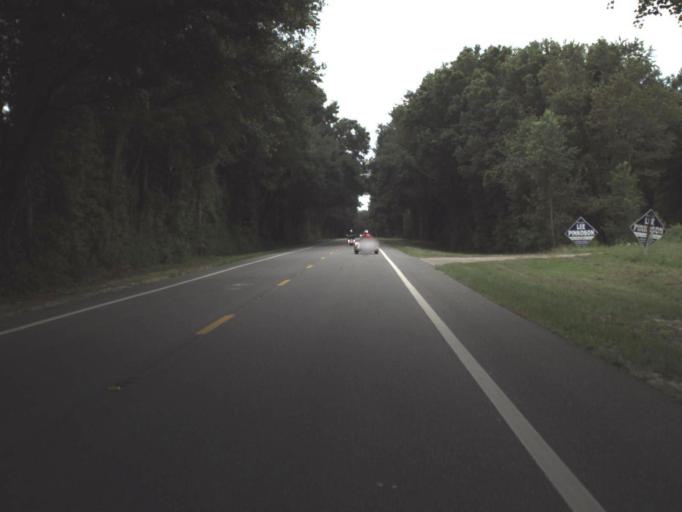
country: US
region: Florida
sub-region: Alachua County
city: Newberry
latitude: 29.6042
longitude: -82.5789
